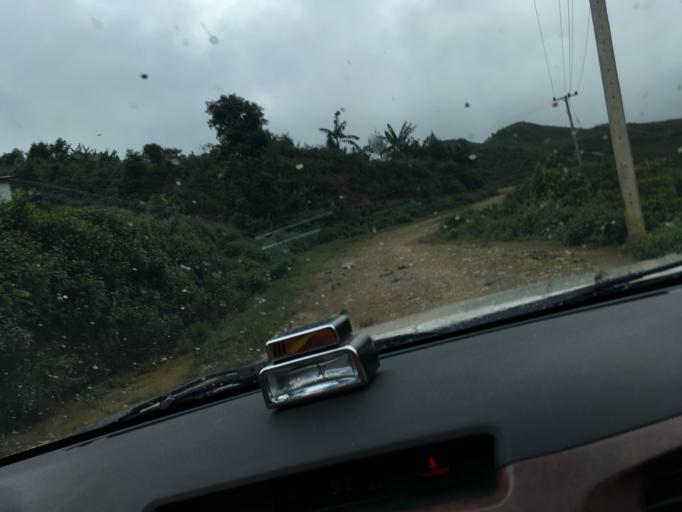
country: LA
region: Phongsali
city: Phongsali
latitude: 21.4041
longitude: 102.2320
